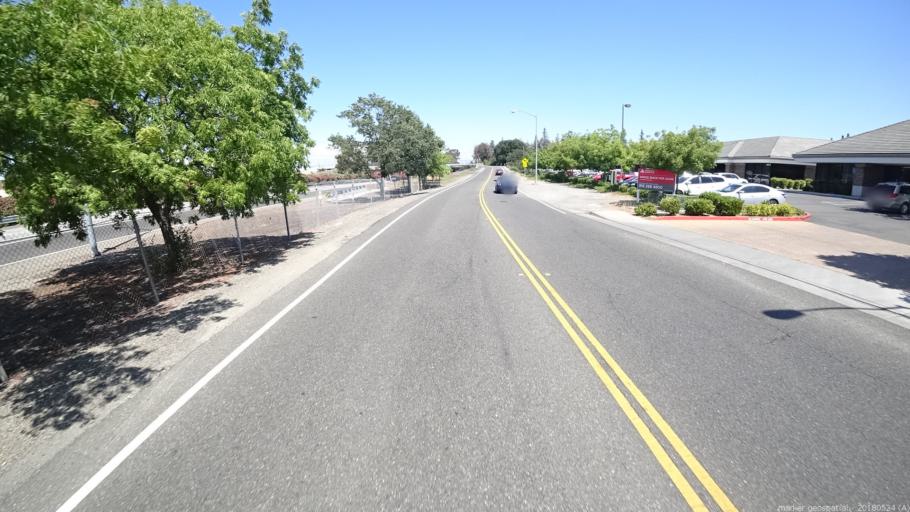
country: US
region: California
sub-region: Sacramento County
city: Sacramento
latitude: 38.5998
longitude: -121.4497
